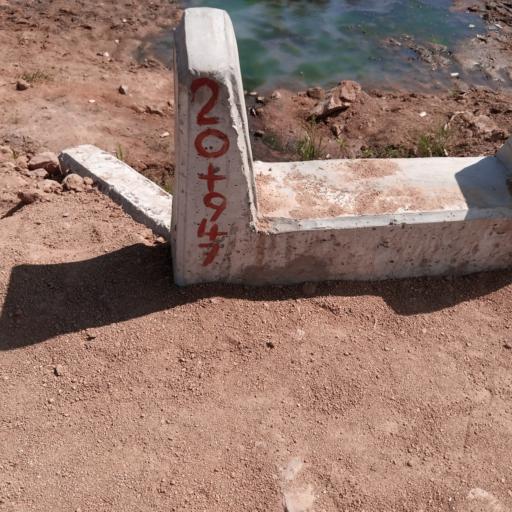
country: NG
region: Adamawa
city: Yola
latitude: 9.0314
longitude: 12.3892
